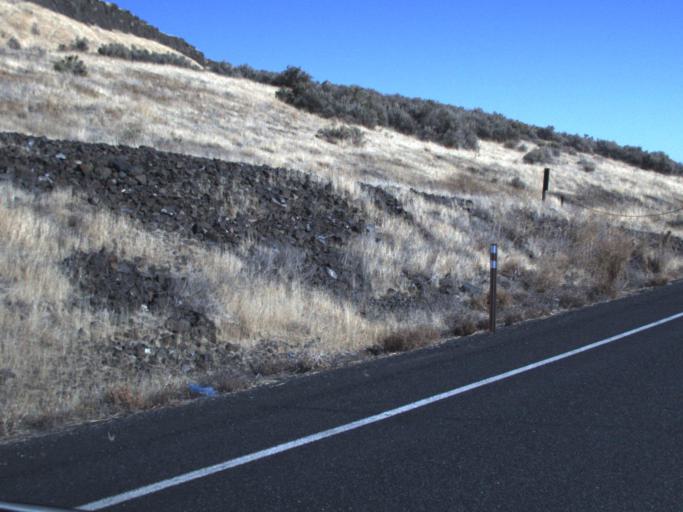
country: US
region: Washington
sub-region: Adams County
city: Ritzville
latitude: 46.9701
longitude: -118.6472
